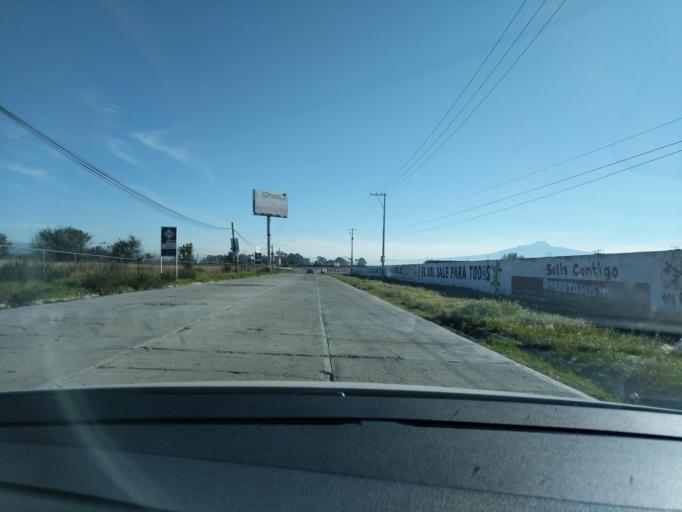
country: MX
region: Puebla
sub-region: Huejotzingo
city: Los Encinos
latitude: 19.1717
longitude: -98.3762
